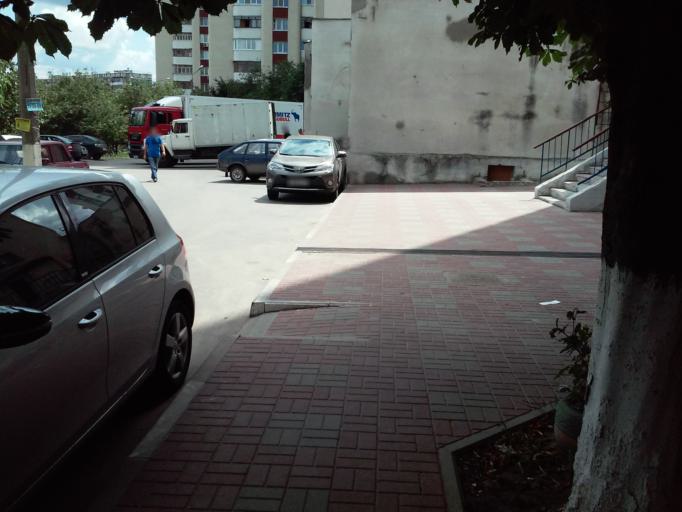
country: RU
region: Belgorod
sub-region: Belgorodskiy Rayon
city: Belgorod
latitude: 50.5745
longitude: 36.5843
